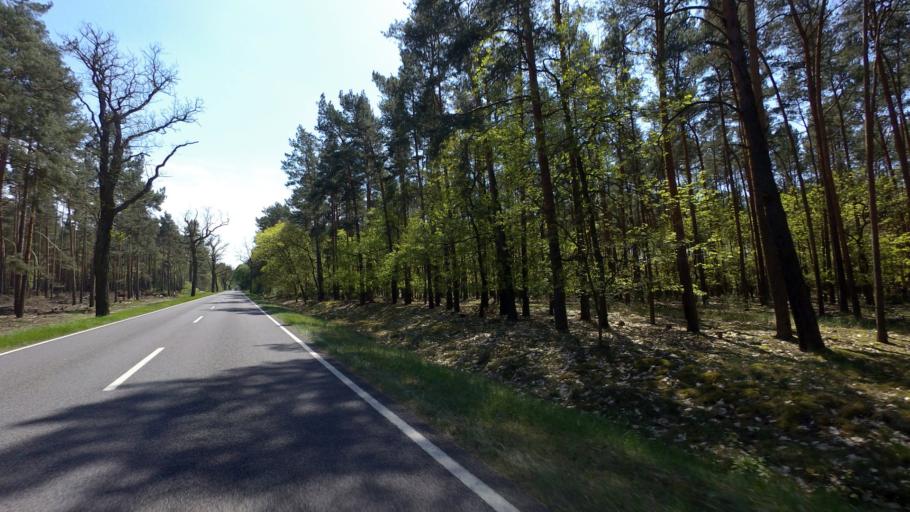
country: DE
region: Brandenburg
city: Halbe
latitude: 52.1621
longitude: 13.7325
